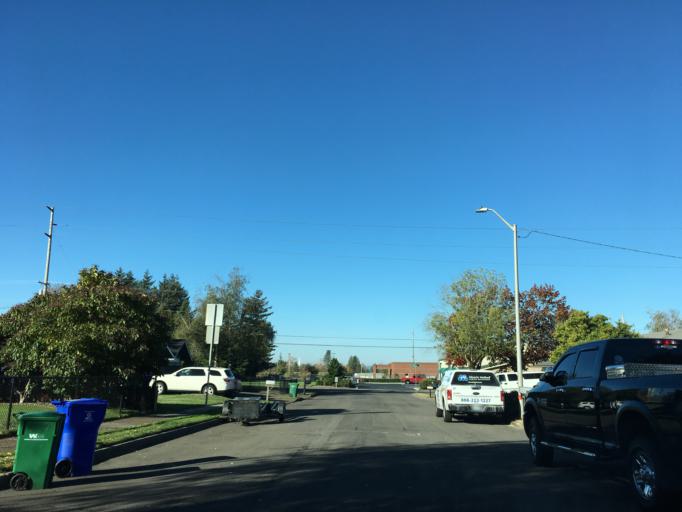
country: US
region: Oregon
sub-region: Multnomah County
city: Wood Village
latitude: 45.5200
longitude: -122.4201
